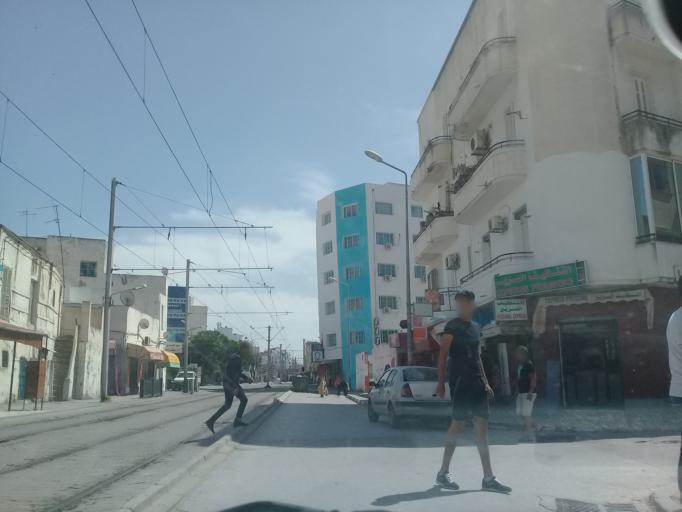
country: TN
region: Tunis
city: Tunis
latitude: 36.8096
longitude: 10.1817
